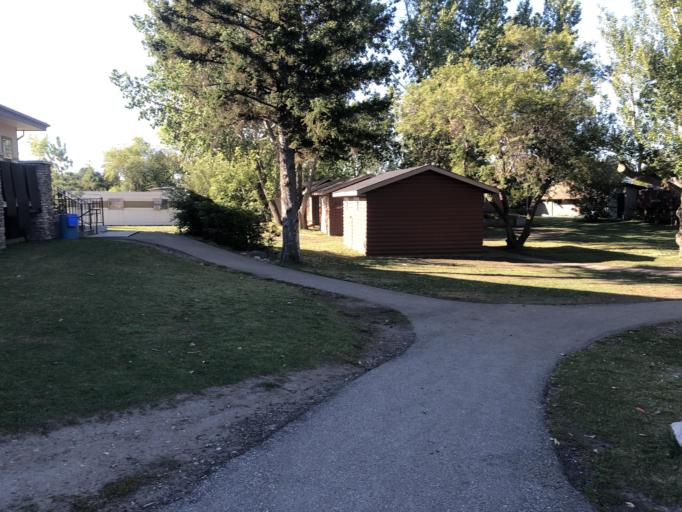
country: CA
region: Alberta
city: Chestermere
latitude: 51.0204
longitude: -113.8169
